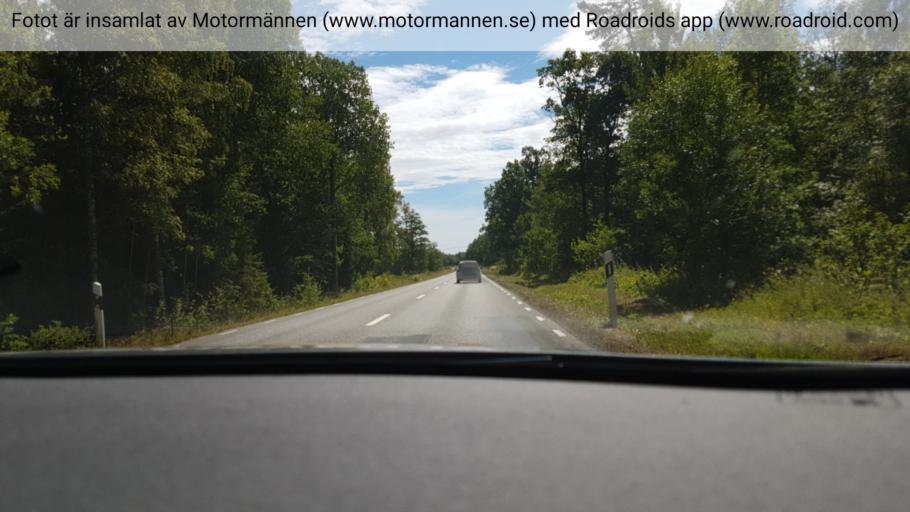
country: SE
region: Joenkoeping
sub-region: Aneby Kommun
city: Aneby
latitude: 57.9796
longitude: 14.7663
